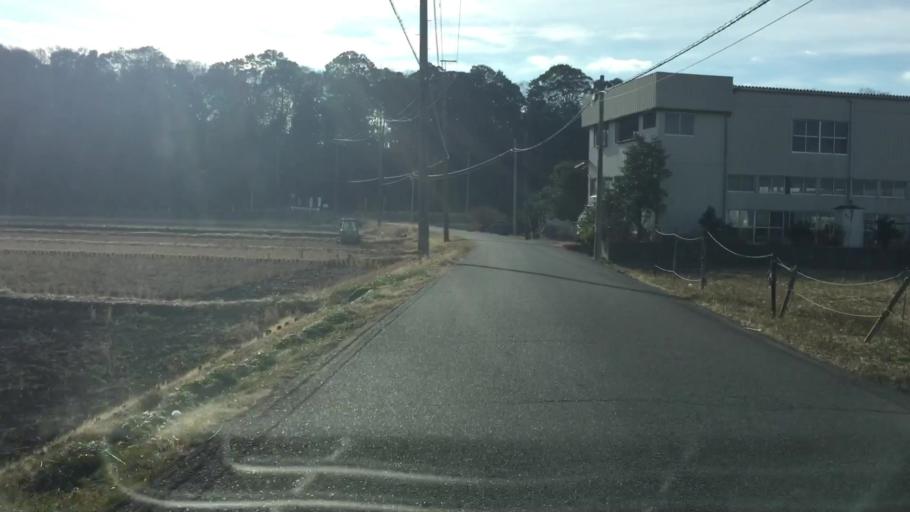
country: JP
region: Chiba
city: Shiroi
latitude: 35.8252
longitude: 140.1217
